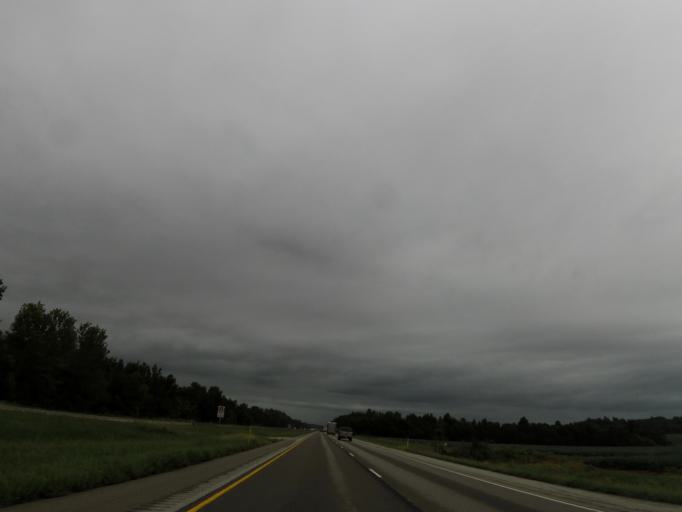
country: US
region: Illinois
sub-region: Massac County
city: Metropolis
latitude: 37.2772
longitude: -88.7449
